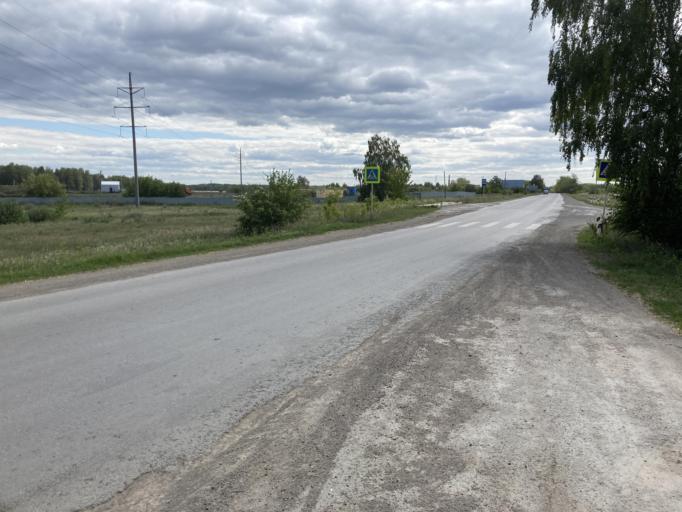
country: RU
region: Sverdlovsk
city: Bogdanovich
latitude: 56.7952
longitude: 62.0687
